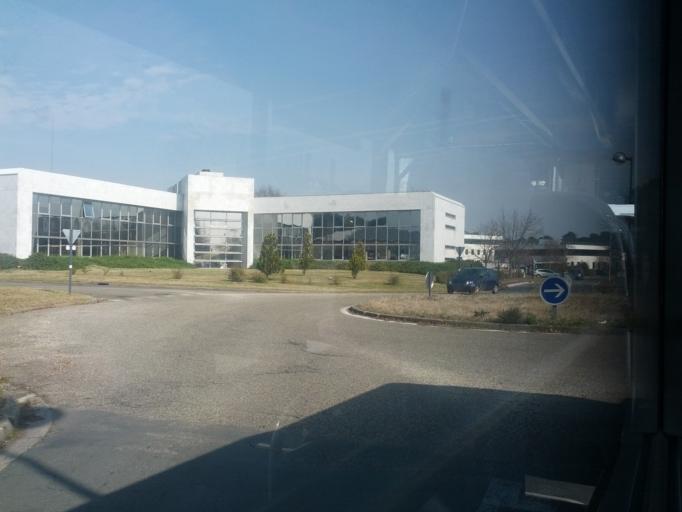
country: FR
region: Aquitaine
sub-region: Departement de la Gironde
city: Le Haillan
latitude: 44.8303
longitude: -0.6856
